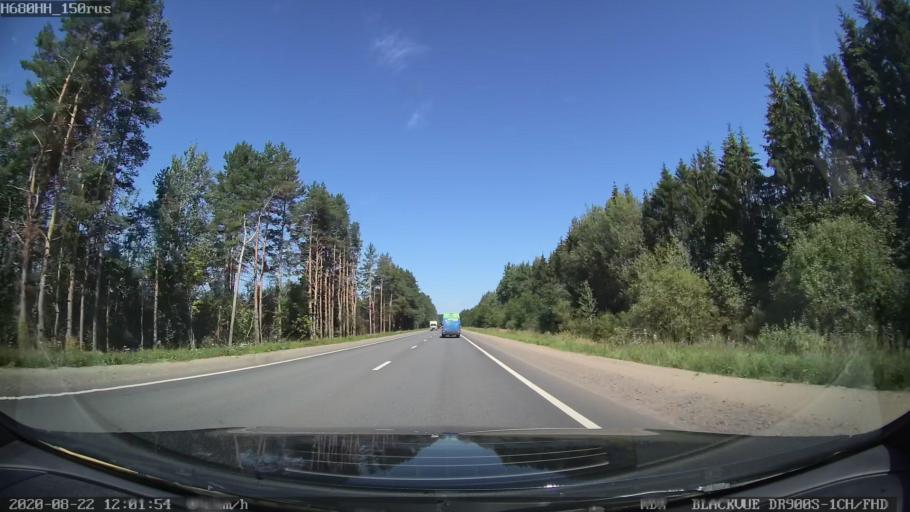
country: RU
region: Tverskaya
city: Rameshki
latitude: 57.2353
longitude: 36.1000
